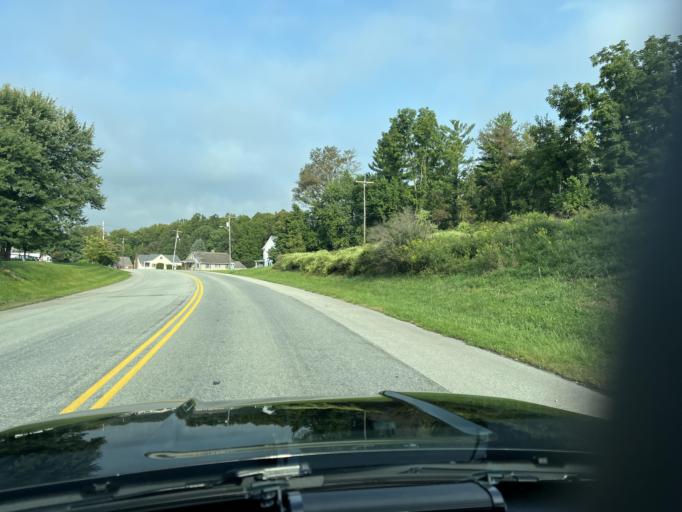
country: US
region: Pennsylvania
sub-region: Fayette County
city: Hopwood
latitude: 39.8729
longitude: -79.7095
